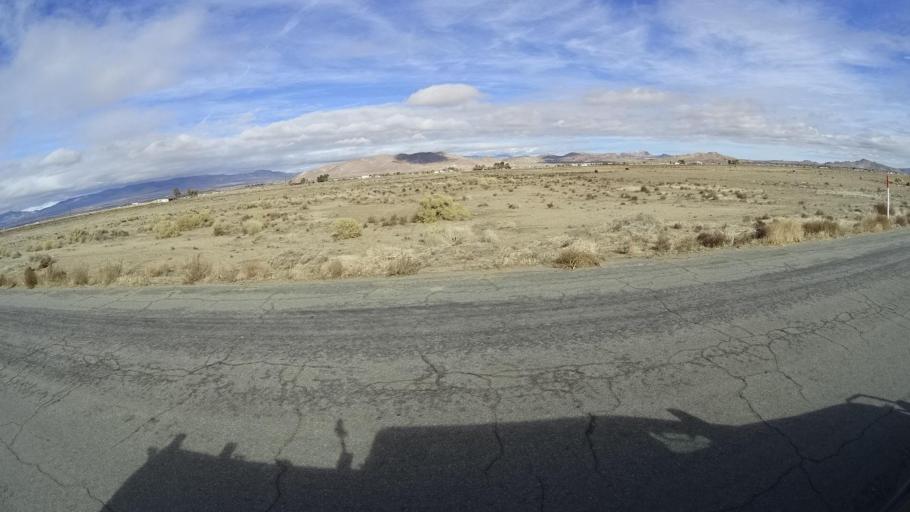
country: US
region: California
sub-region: Kern County
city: Rosamond
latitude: 34.8345
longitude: -118.2703
